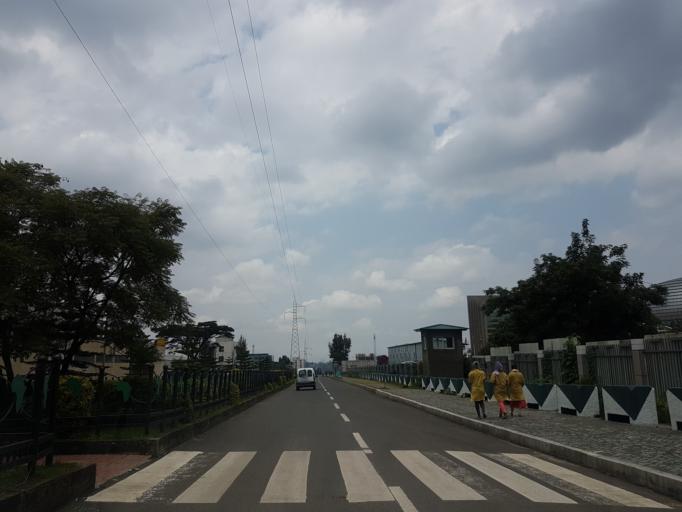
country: ET
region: Adis Abeba
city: Addis Ababa
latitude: 9.0021
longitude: 38.7455
